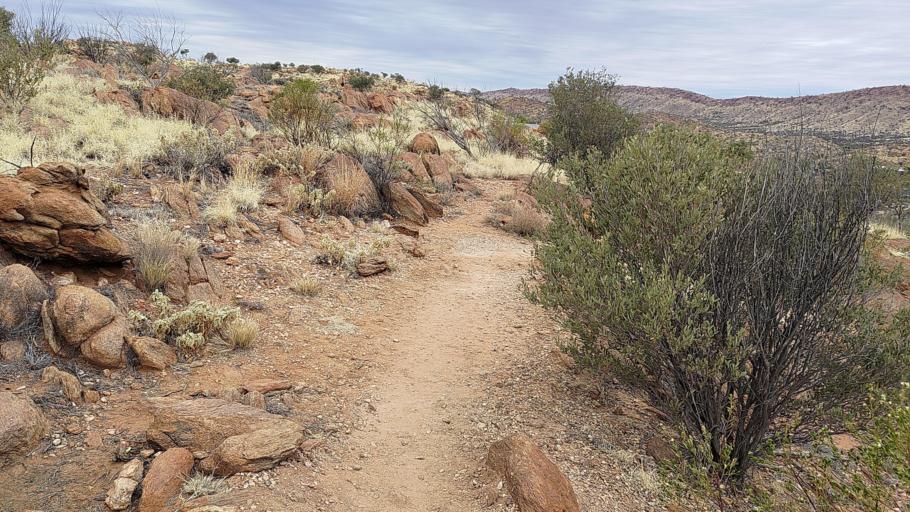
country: AU
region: Northern Territory
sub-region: Alice Springs
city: Alice Springs
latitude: -23.7054
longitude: 133.8856
